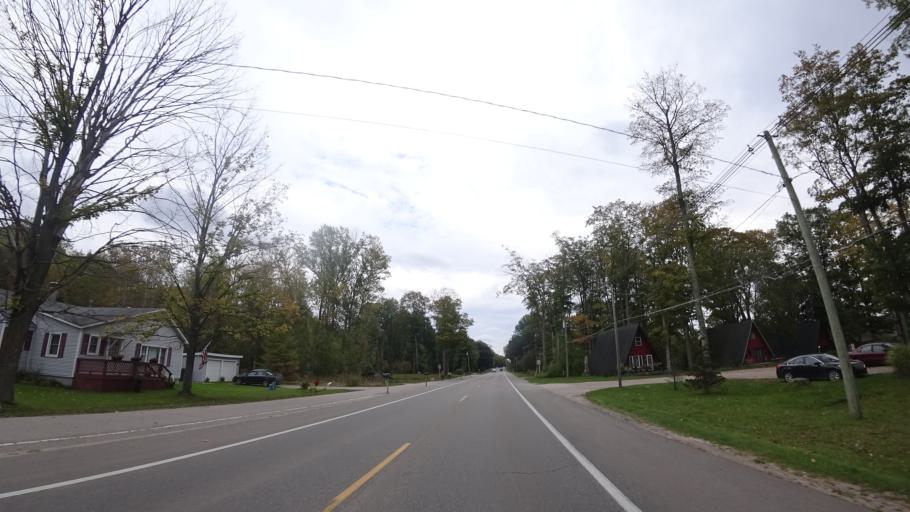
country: US
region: Michigan
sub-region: Emmet County
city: Harbor Springs
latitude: 45.4311
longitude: -84.9337
